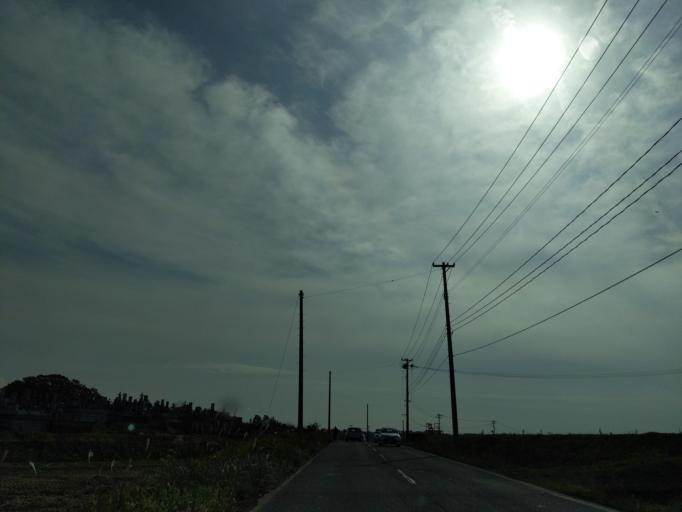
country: JP
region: Fukushima
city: Koriyama
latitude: 37.4327
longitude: 140.3138
